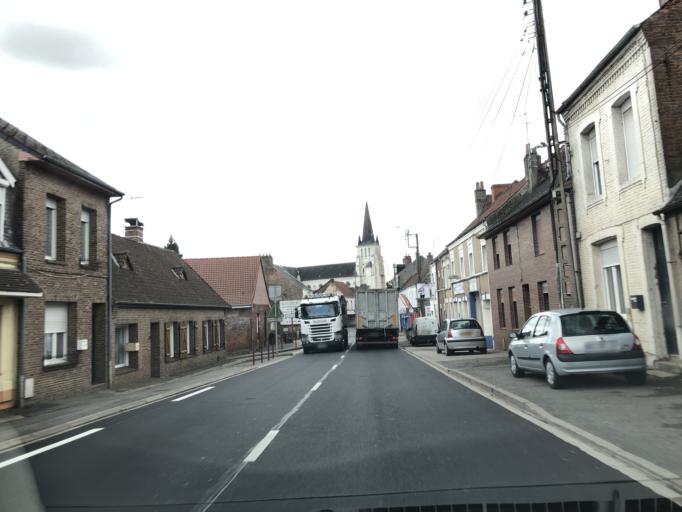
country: FR
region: Nord-Pas-de-Calais
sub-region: Departement du Pas-de-Calais
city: Fruges
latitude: 50.5173
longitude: 2.1344
